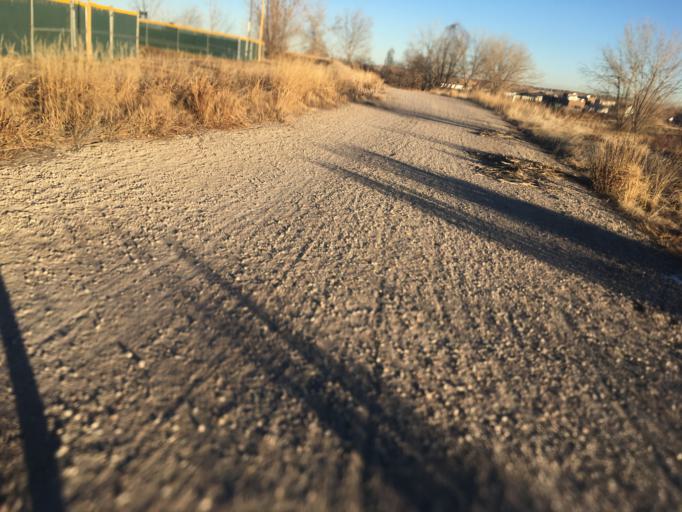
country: US
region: Colorado
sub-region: Boulder County
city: Louisville
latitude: 39.9808
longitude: -105.1256
